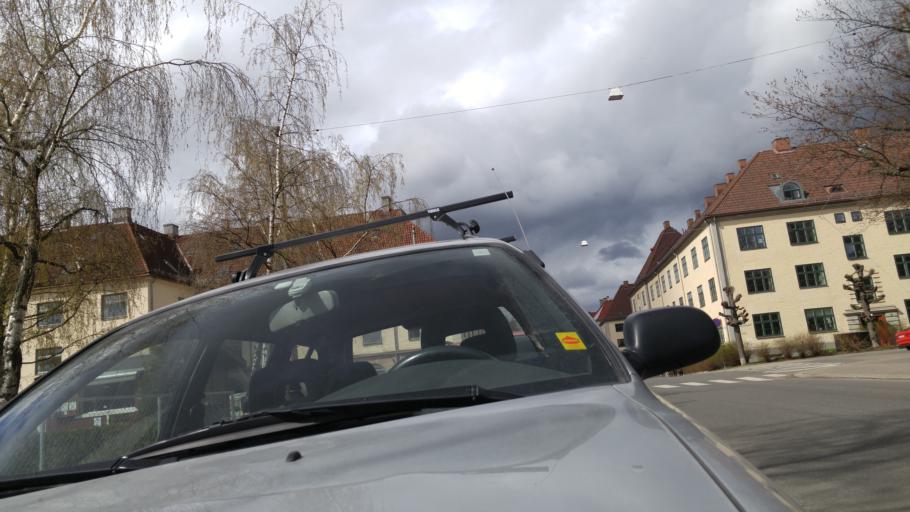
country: NO
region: Oslo
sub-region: Oslo
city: Oslo
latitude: 59.9341
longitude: 10.7689
